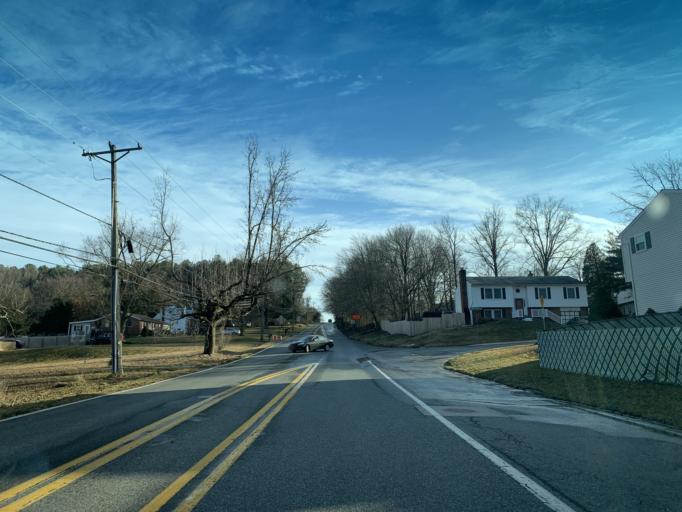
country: US
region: Delaware
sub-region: New Castle County
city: Bear
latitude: 39.6717
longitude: -75.6584
